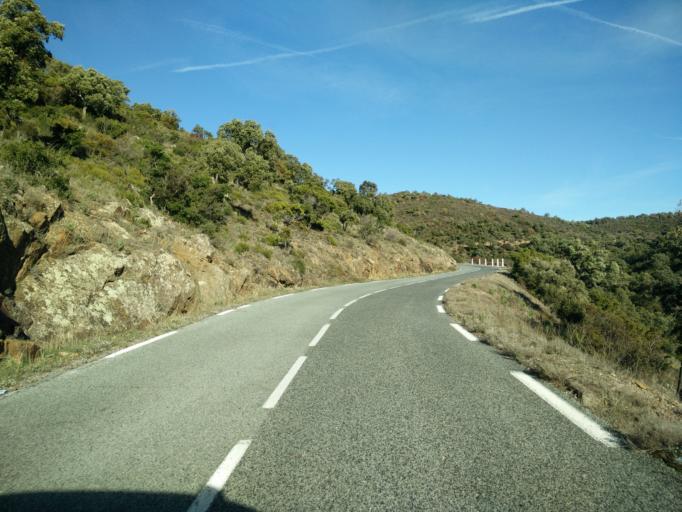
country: FR
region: Provence-Alpes-Cote d'Azur
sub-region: Departement du Var
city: Saint-Raphael
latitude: 43.4968
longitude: 6.7810
